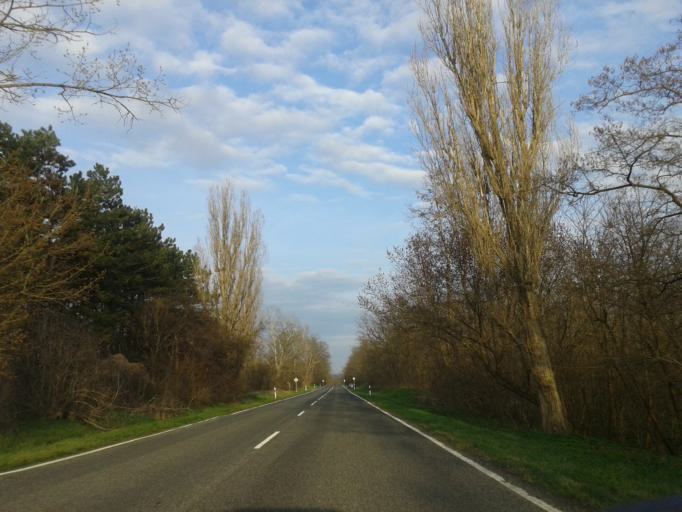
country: HU
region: Gyor-Moson-Sopron
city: Bony
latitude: 47.7330
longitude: 17.8827
